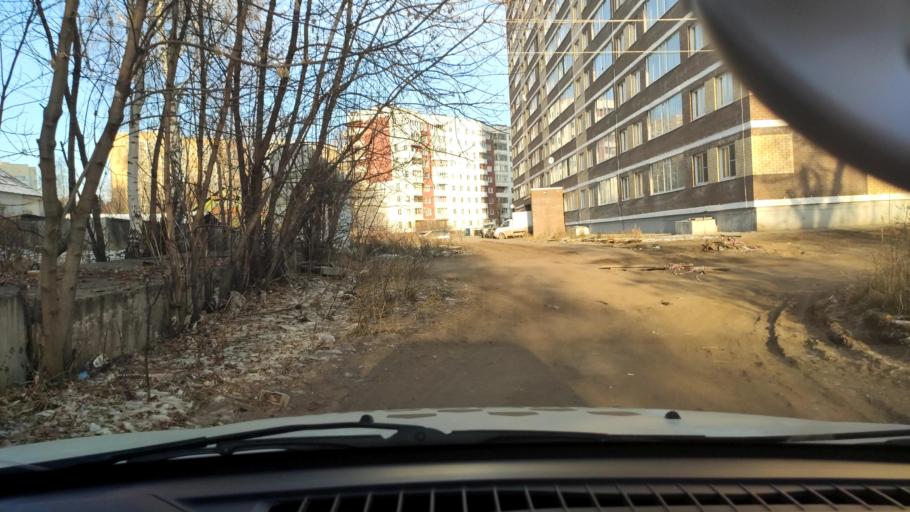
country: RU
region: Perm
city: Kondratovo
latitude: 58.0308
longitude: 56.0245
